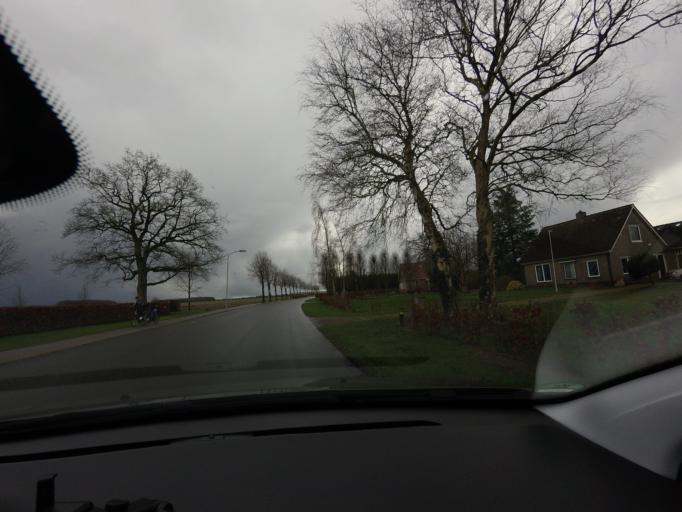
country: NL
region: Drenthe
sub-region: Gemeente Borger-Odoorn
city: Borger
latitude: 52.9502
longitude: 6.7906
